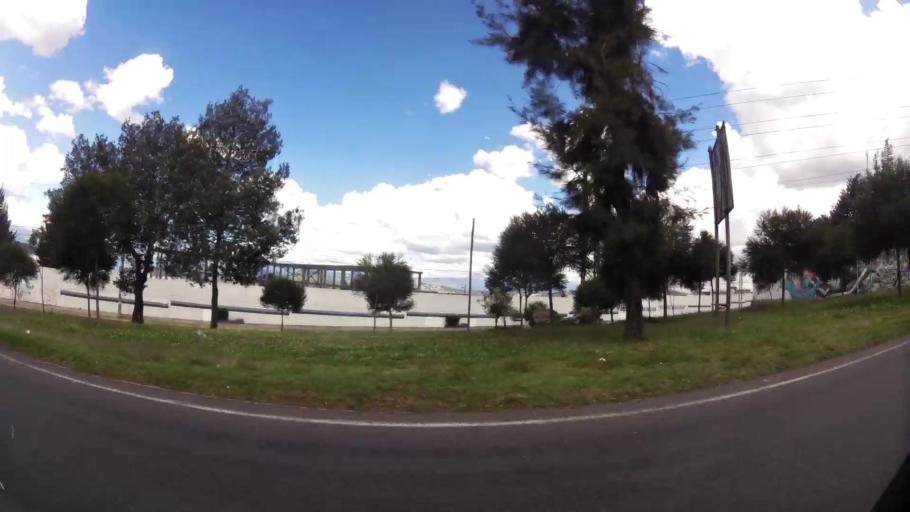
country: EC
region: Pichincha
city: Quito
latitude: -0.1827
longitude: -78.5062
